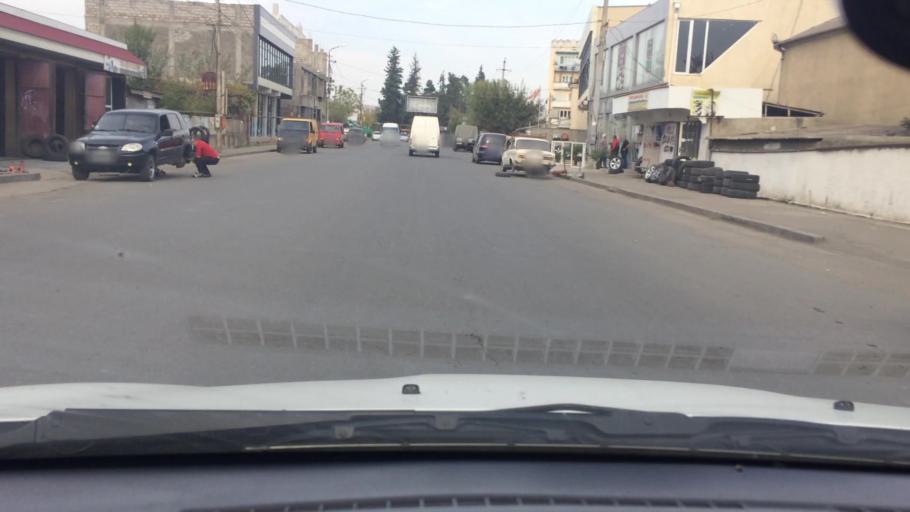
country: GE
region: Kvemo Kartli
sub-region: Marneuli
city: Marneuli
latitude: 41.4665
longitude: 44.8169
